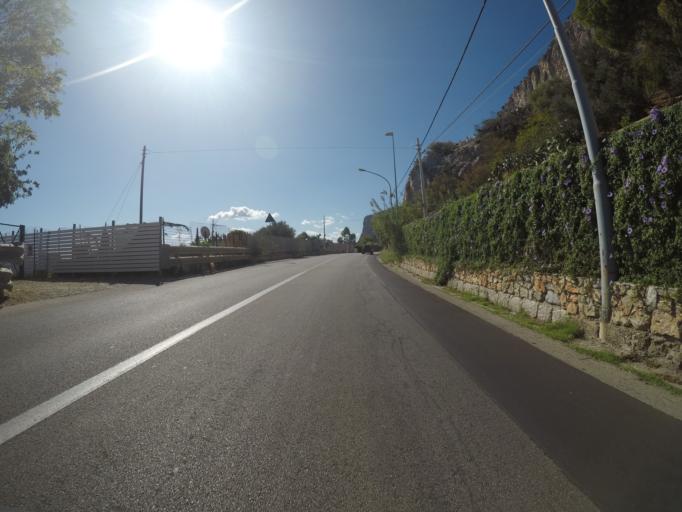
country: IT
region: Sicily
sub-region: Palermo
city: Palermo
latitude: 38.1787
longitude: 13.3662
